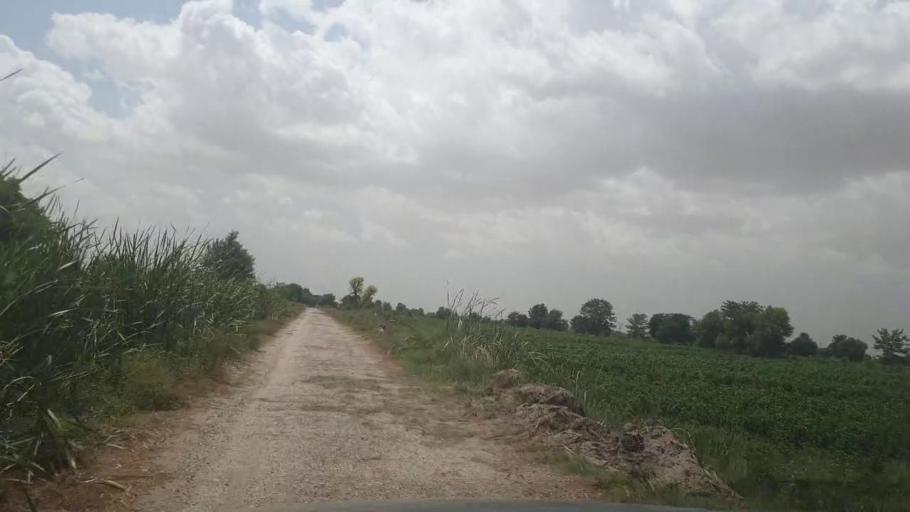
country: PK
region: Sindh
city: Kot Diji
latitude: 27.2351
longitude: 69.0120
